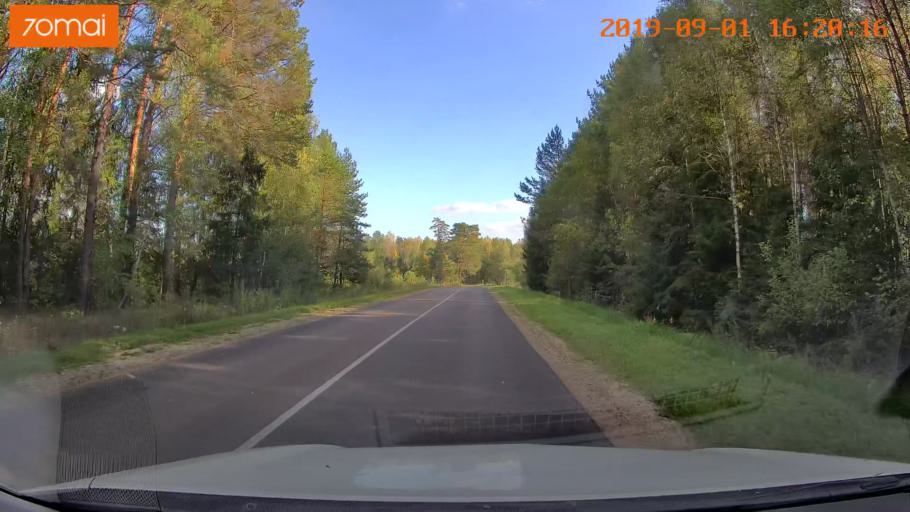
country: RU
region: Kaluga
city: Maloyaroslavets
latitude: 54.8808
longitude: 36.5332
